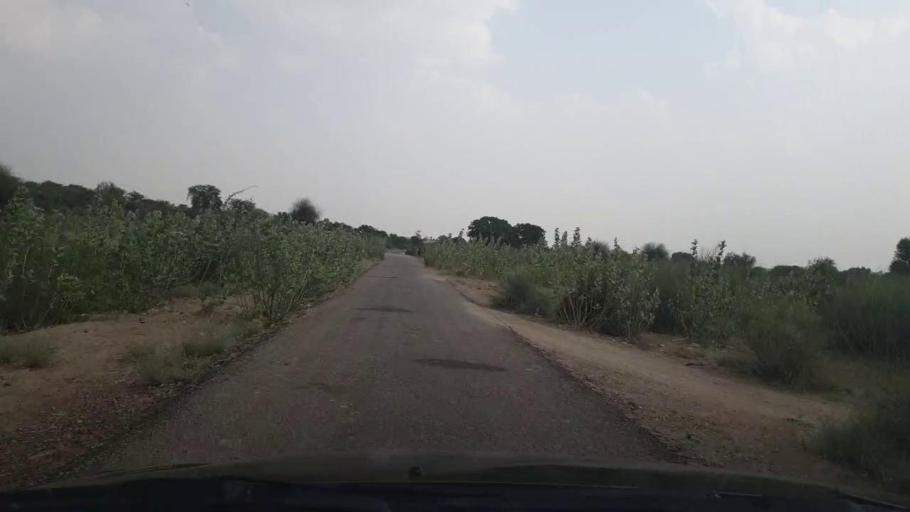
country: PK
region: Sindh
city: Islamkot
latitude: 25.0056
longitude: 70.5985
